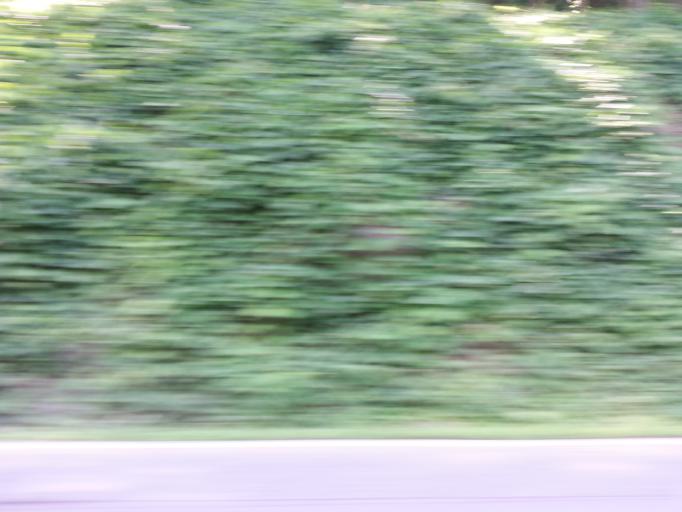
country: US
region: Virginia
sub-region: Lee County
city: Pennington Gap
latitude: 36.7755
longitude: -83.0332
